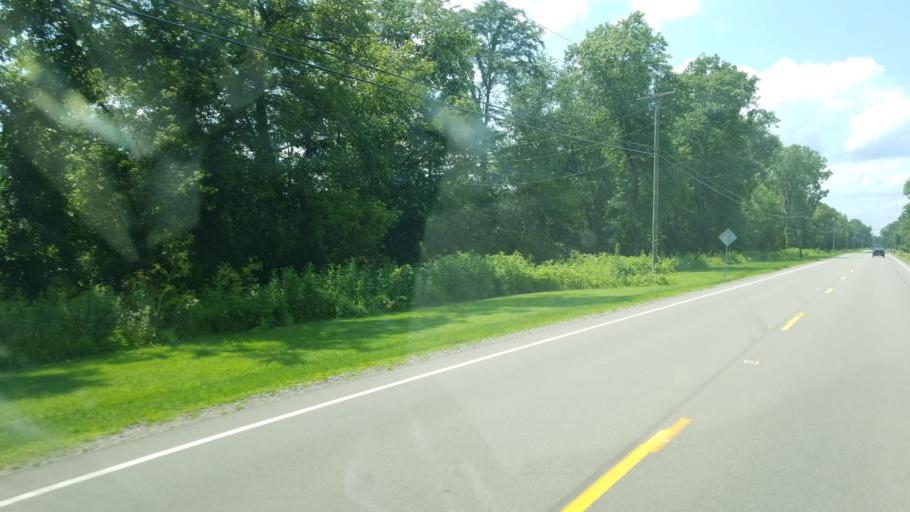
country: US
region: Ohio
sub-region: Coshocton County
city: Coshocton
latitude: 40.3100
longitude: -81.9298
